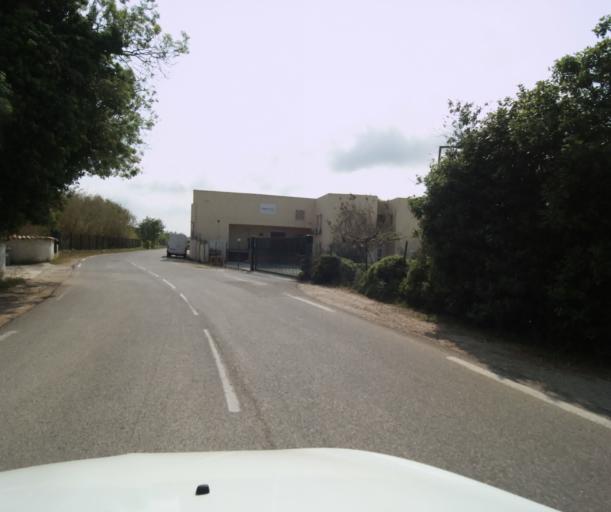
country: FR
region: Provence-Alpes-Cote d'Azur
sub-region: Departement du Var
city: Hyeres
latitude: 43.1044
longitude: 6.1443
